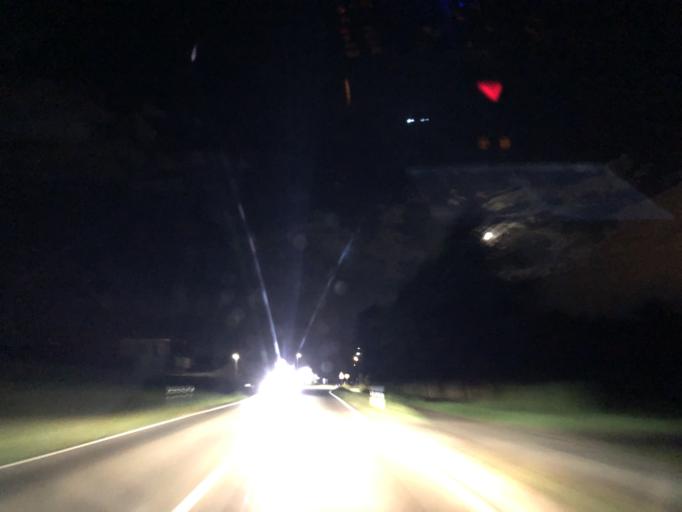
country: DE
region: Bavaria
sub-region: Upper Bavaria
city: Finsing
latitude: 48.2318
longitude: 11.8151
